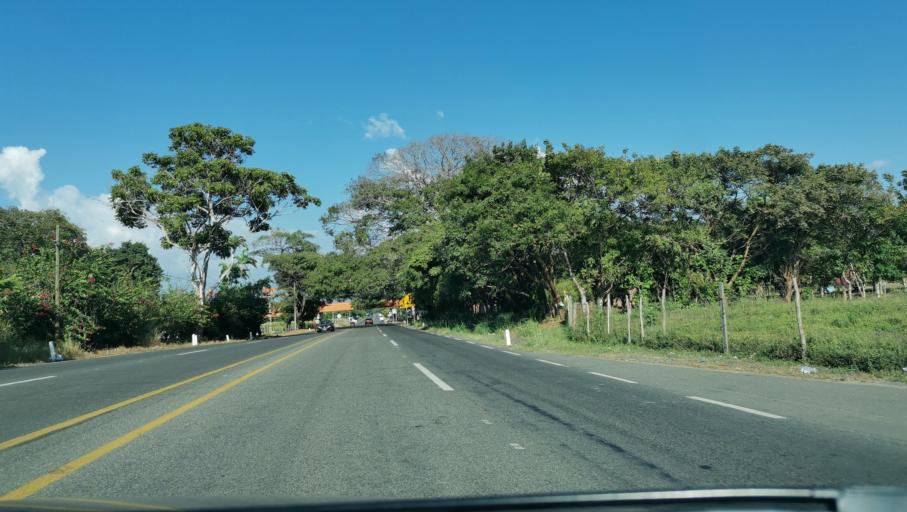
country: MX
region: Chiapas
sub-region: Tapachula
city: Congregacion Reforma
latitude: 14.8171
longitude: -92.3430
